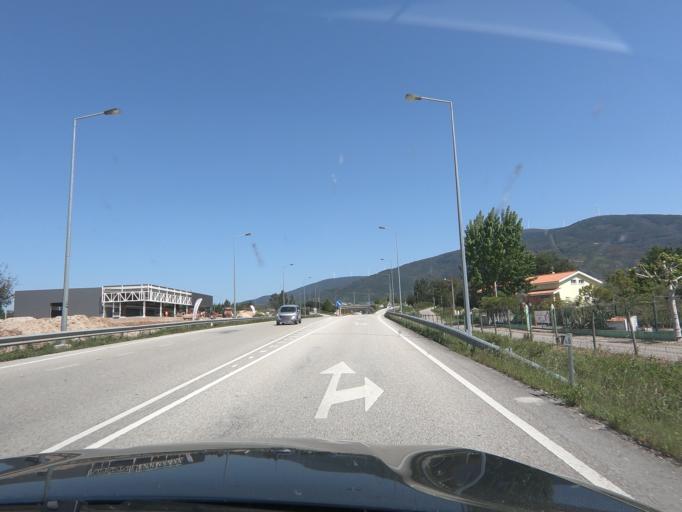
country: PT
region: Coimbra
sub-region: Lousa
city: Lousa
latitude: 40.1289
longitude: -8.2520
